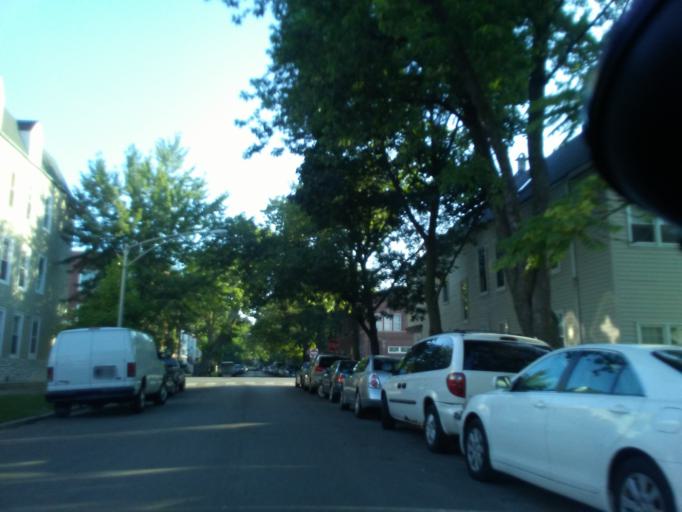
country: US
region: Illinois
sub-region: Cook County
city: Lincolnwood
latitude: 41.9315
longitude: -87.7208
